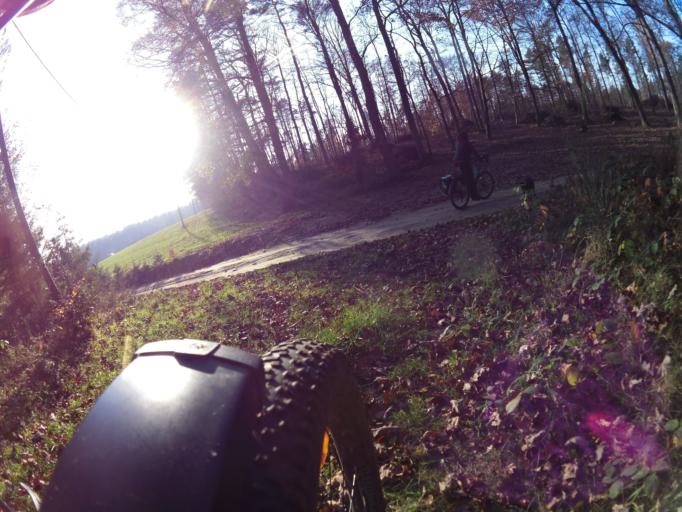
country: PL
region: Pomeranian Voivodeship
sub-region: Powiat pucki
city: Krokowa
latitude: 54.7272
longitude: 18.2086
